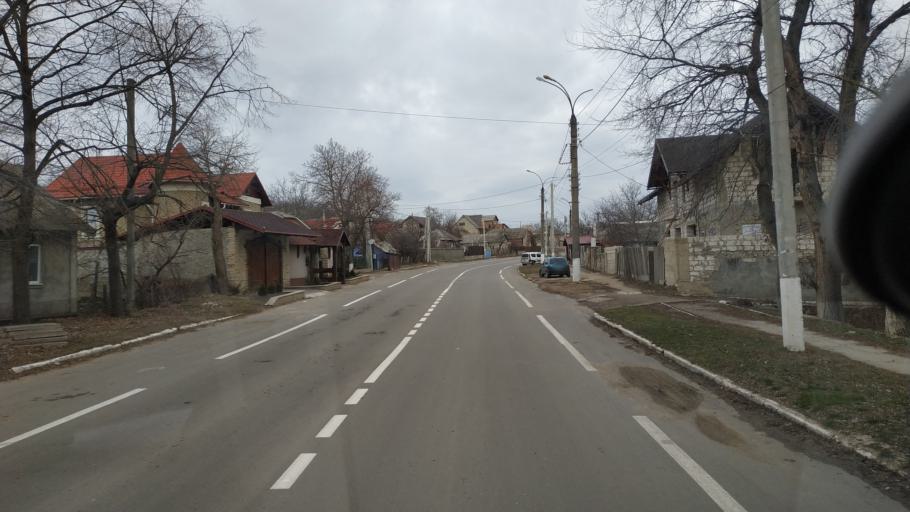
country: MD
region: Criuleni
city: Criuleni
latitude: 47.2177
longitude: 29.1632
